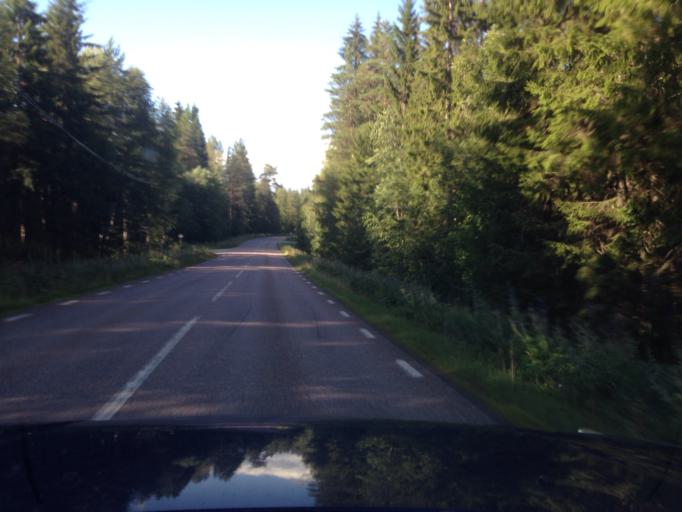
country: SE
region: Dalarna
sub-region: Ludvika Kommun
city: Grangesberg
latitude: 60.1363
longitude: 15.0613
